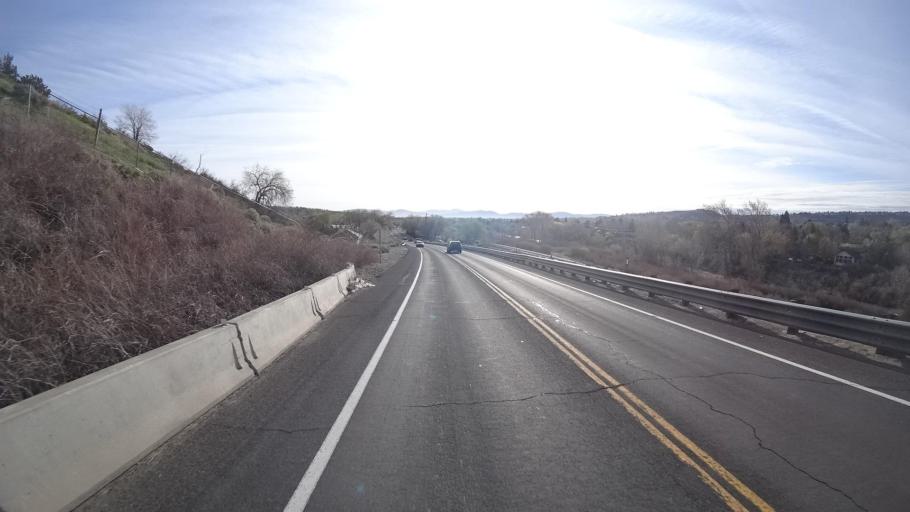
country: US
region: Nevada
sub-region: Washoe County
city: Mogul
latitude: 39.5109
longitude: -119.8723
